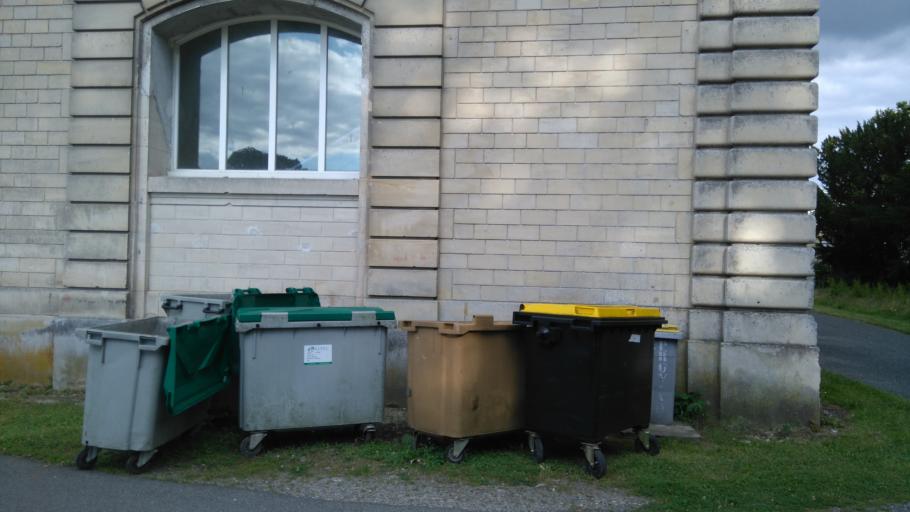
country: FR
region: Picardie
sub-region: Departement de l'Oise
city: Saint-Maximin
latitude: 49.2357
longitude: 2.4589
